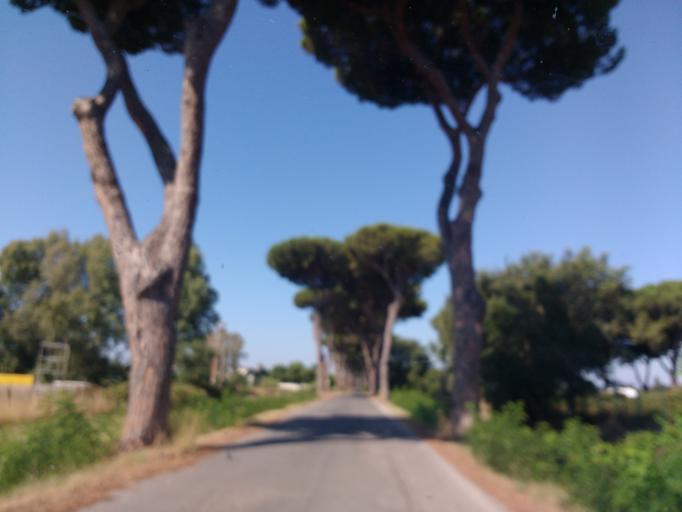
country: IT
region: Latium
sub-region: Citta metropolitana di Roma Capitale
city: Acilia-Castel Fusano-Ostia Antica
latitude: 41.7543
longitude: 12.3405
